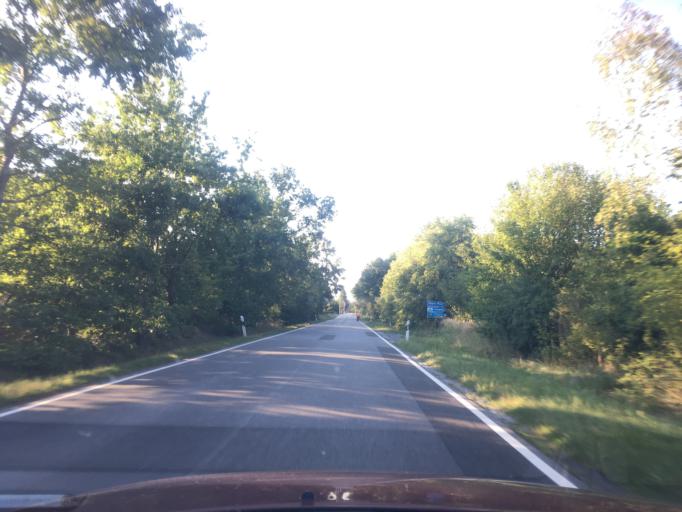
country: DE
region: Saxony
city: Rothenburg
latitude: 51.3245
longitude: 14.9748
